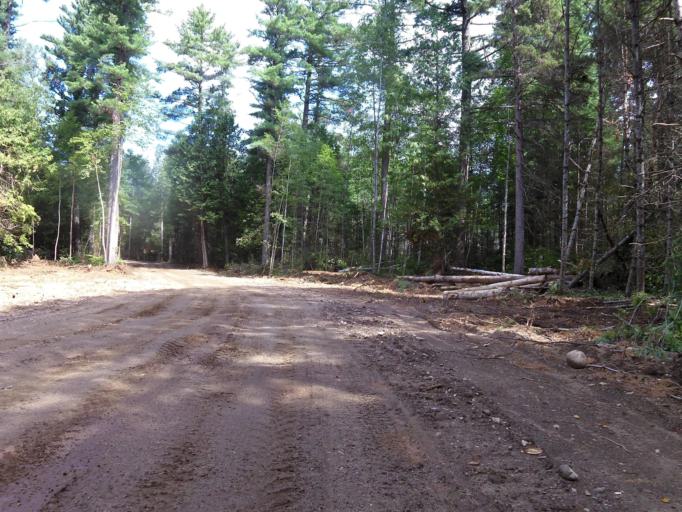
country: CA
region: Ontario
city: Renfrew
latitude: 45.1102
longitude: -76.7241
